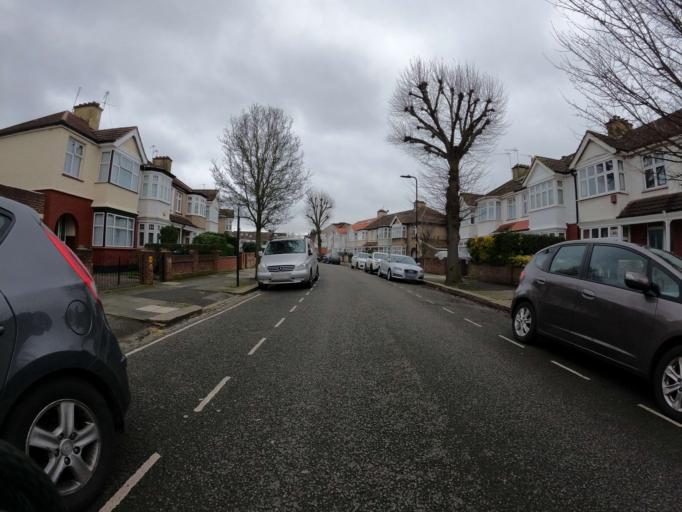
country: GB
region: England
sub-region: Greater London
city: Ealing
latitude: 51.5057
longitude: -0.3281
